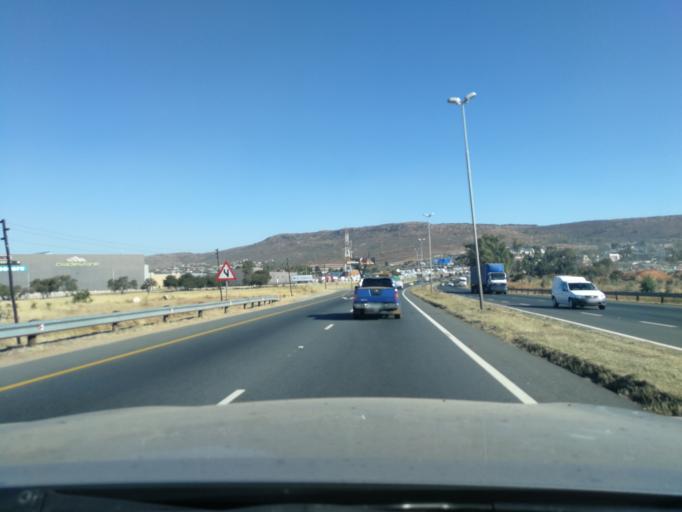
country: ZA
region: Gauteng
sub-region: West Rand District Municipality
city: Muldersdriseloop
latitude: -26.0570
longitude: 27.8360
